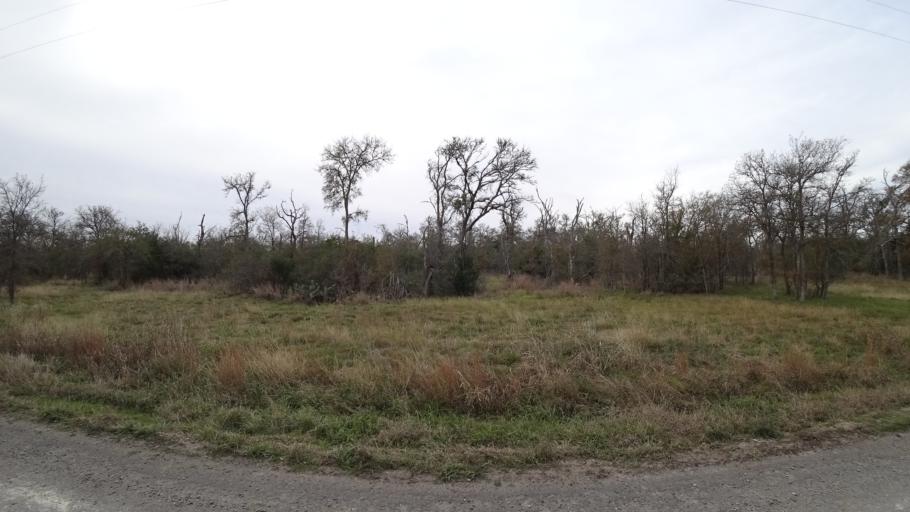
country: US
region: Texas
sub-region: Travis County
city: Garfield
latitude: 30.1083
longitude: -97.5719
